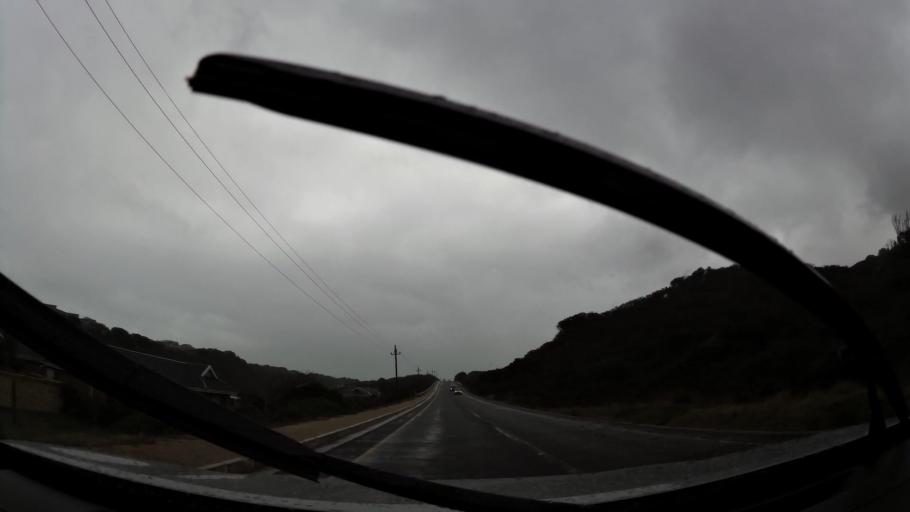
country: ZA
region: Western Cape
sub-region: Eden District Municipality
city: Mossel Bay
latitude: -34.0520
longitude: 22.2531
